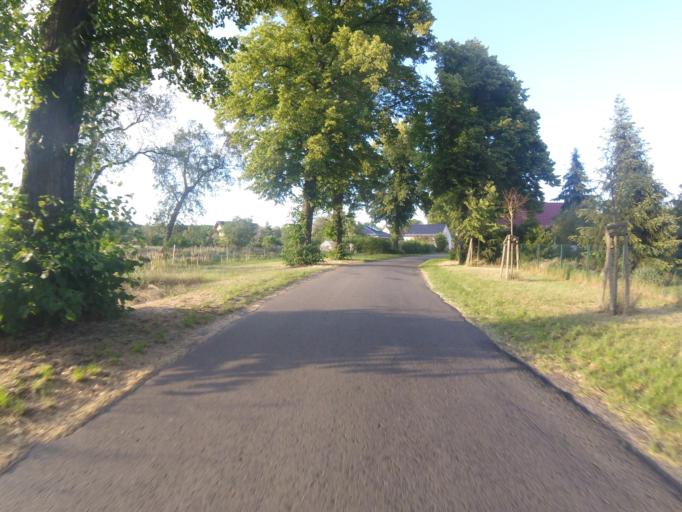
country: DE
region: Brandenburg
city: Mittenwalde
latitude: 52.2424
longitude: 13.5571
